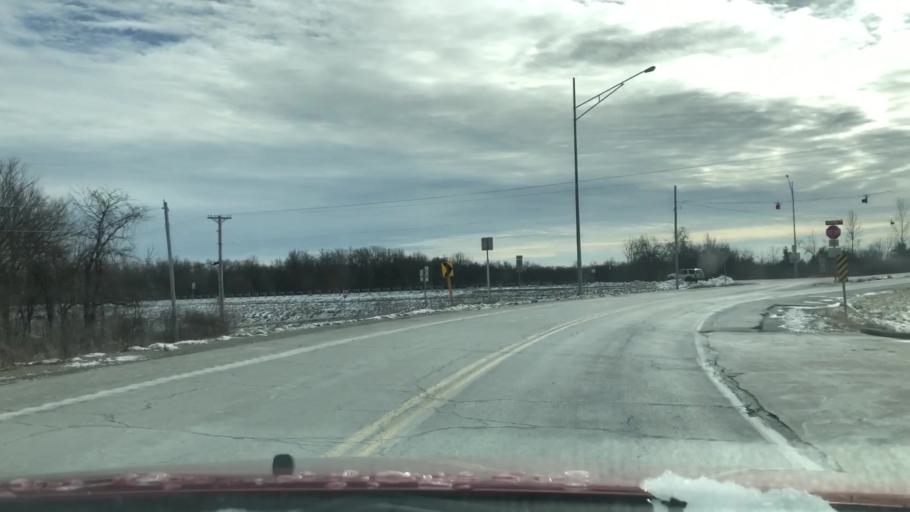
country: US
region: Missouri
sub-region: Jackson County
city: Lone Jack
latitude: 38.8711
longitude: -94.1337
